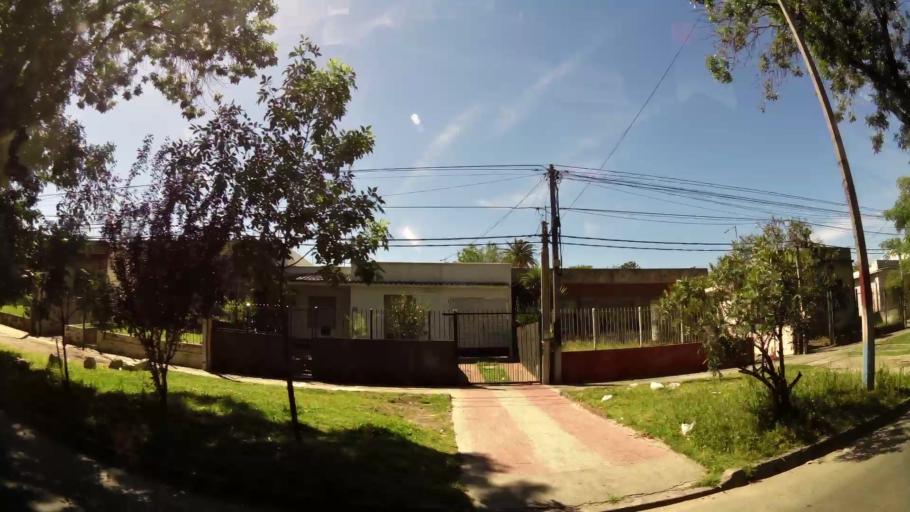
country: UY
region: Canelones
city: Paso de Carrasco
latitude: -34.8504
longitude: -56.1277
